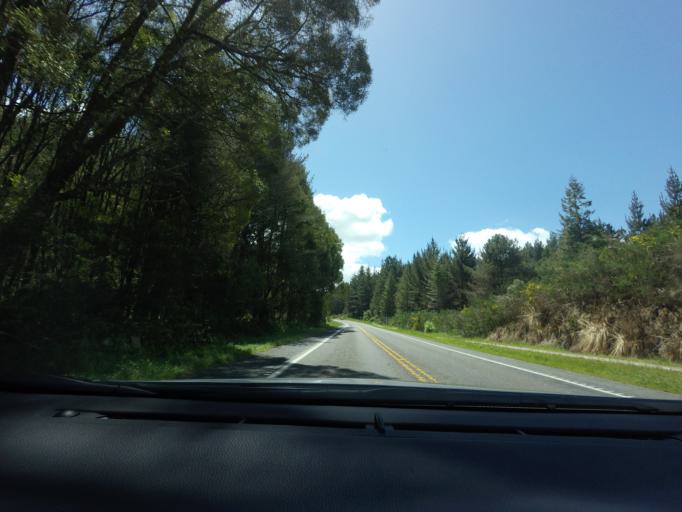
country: NZ
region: Bay of Plenty
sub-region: Rotorua District
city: Rotorua
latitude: -38.1911
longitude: 176.2595
